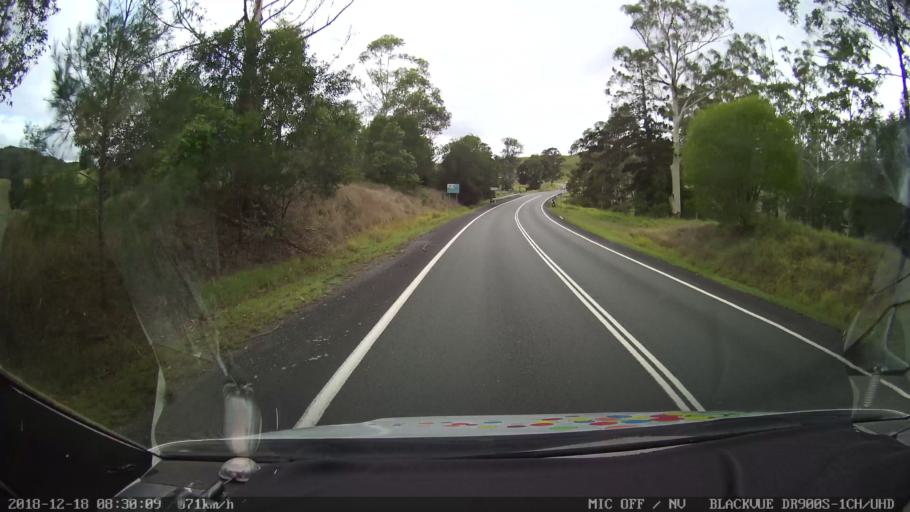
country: AU
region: New South Wales
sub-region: Kyogle
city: Kyogle
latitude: -28.3227
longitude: 152.7661
